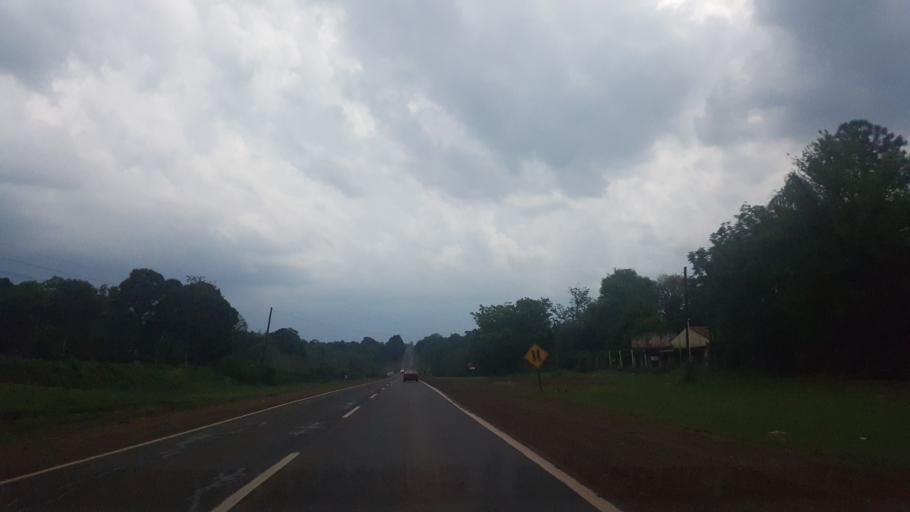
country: AR
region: Misiones
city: Santo Pipo
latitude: -27.1195
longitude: -55.3710
